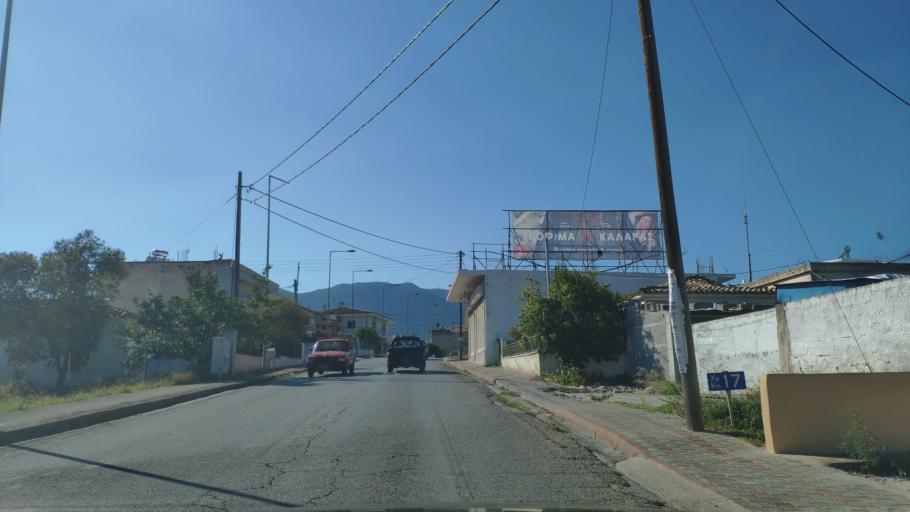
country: GR
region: Peloponnese
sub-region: Nomos Korinthias
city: Khiliomodhi
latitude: 37.8137
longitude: 22.8712
